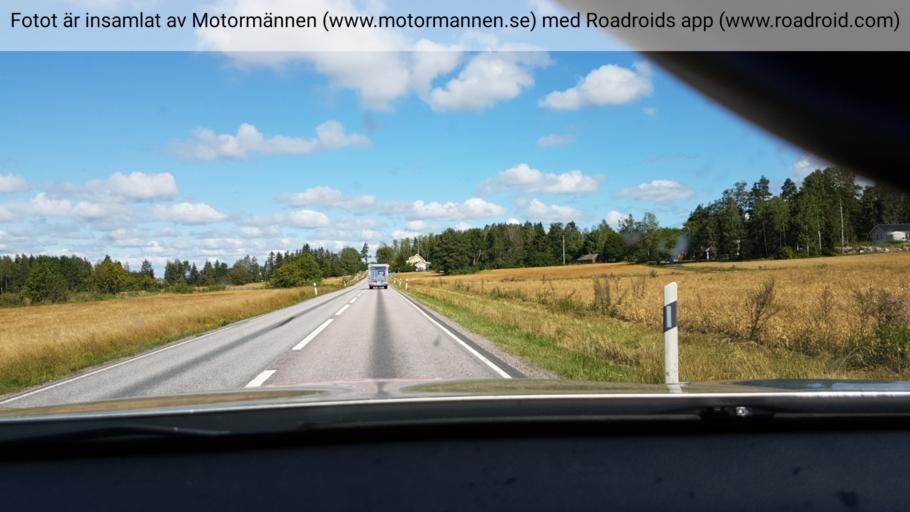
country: SE
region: Stockholm
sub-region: Norrtalje Kommun
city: Norrtalje
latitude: 59.7806
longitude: 18.6709
